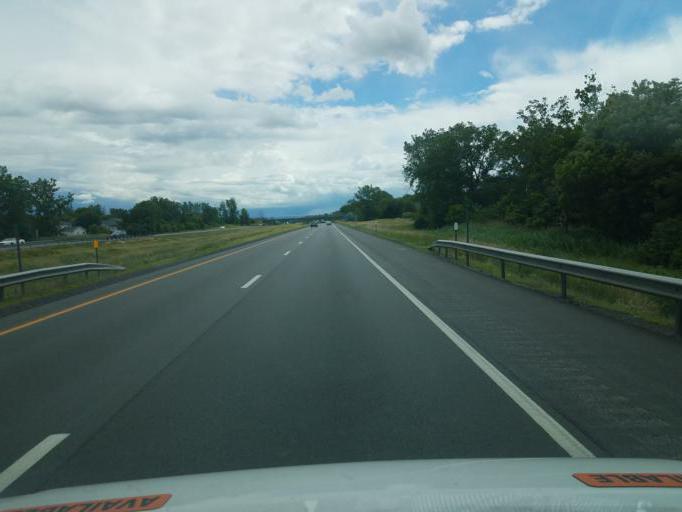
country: US
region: New York
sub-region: Monroe County
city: Scottsville
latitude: 43.0419
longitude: -77.7022
